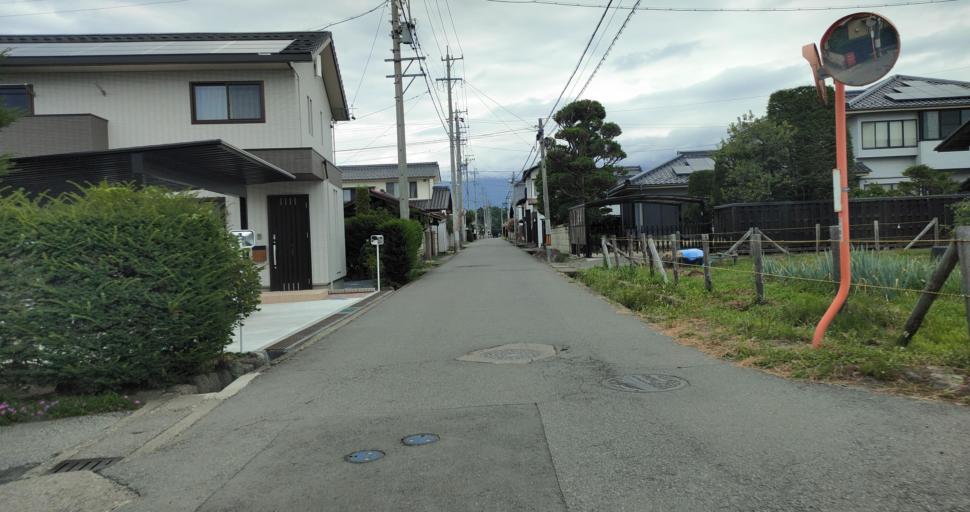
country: JP
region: Nagano
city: Komoro
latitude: 36.2902
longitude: 138.4588
